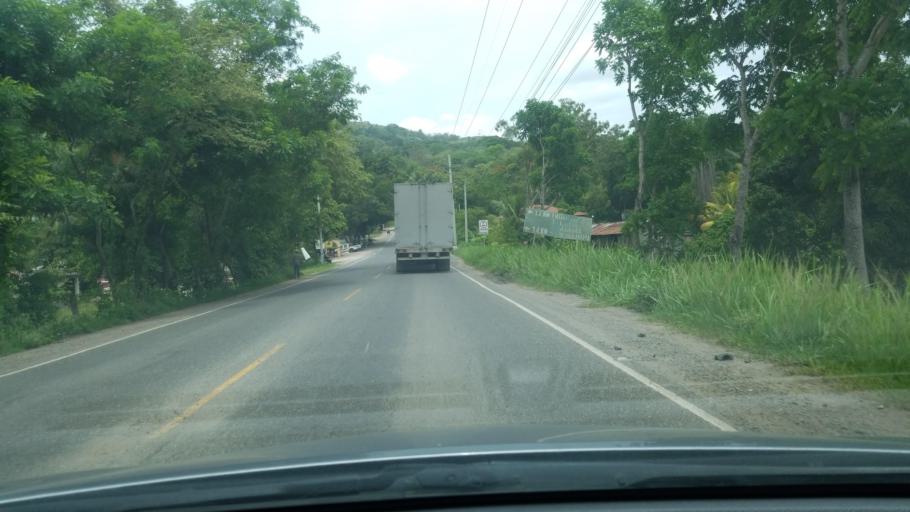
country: HN
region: Copan
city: Ojos de Agua
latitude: 14.7153
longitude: -88.7791
